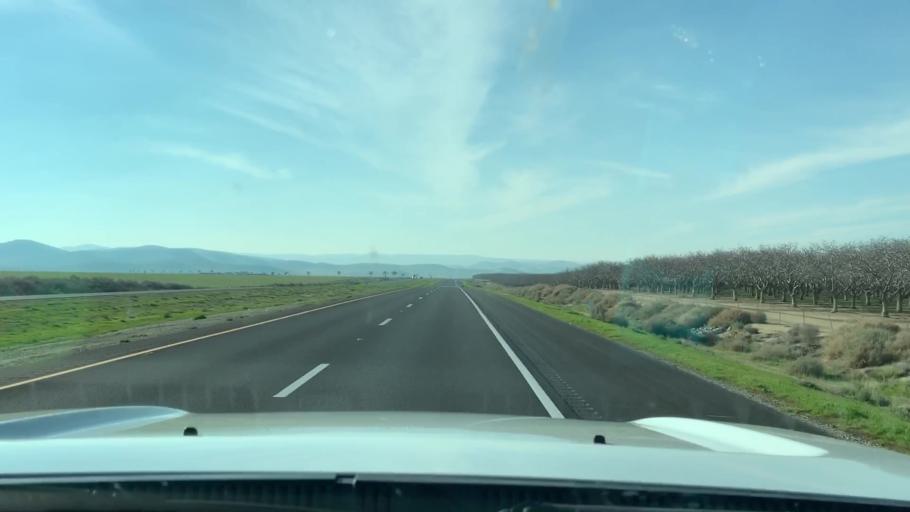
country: US
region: California
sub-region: Kern County
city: Lost Hills
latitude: 35.6134
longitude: -119.9499
